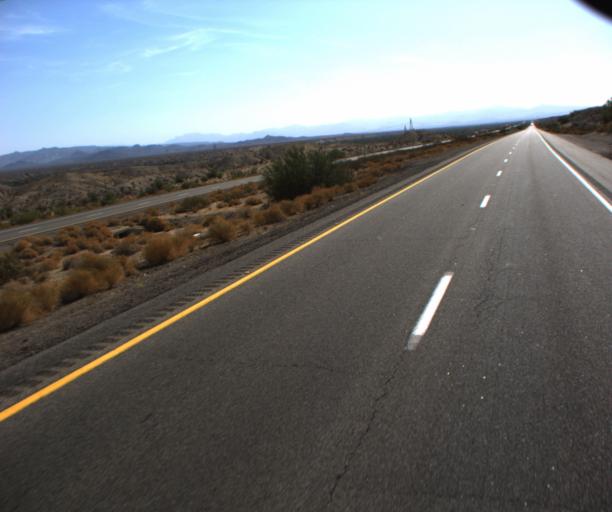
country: US
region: Arizona
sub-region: Mohave County
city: Desert Hills
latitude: 34.7265
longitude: -114.3951
